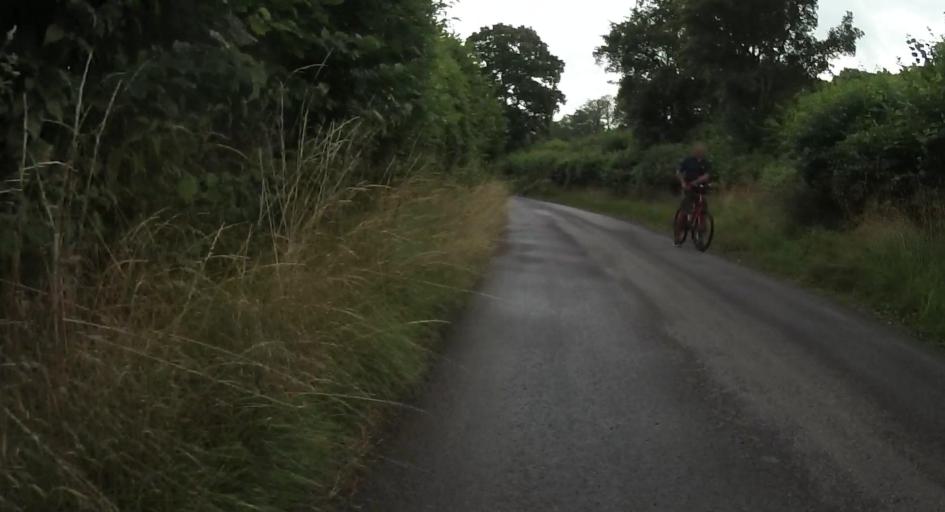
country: GB
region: England
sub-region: Hampshire
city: Andover
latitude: 51.2061
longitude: -1.4283
